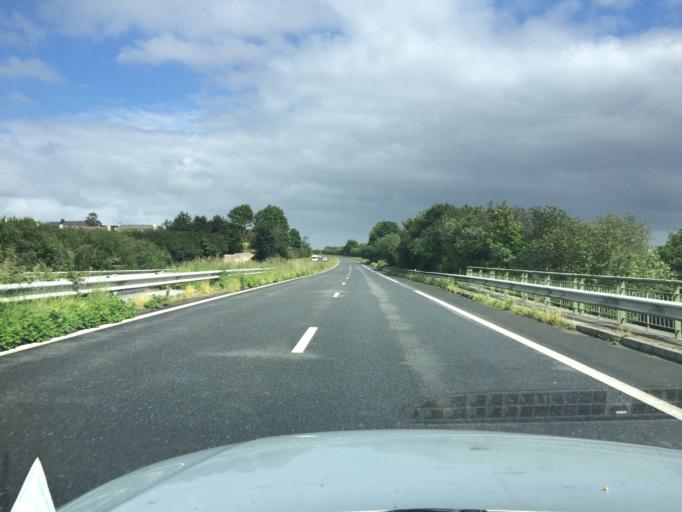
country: FR
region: Brittany
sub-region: Departement du Finistere
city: Plouedern
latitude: 48.4885
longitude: -4.2460
